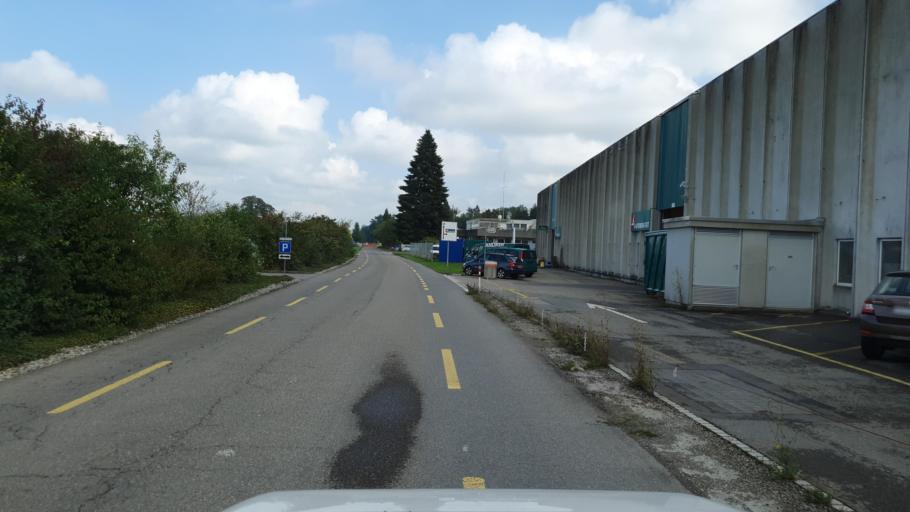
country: CH
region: Lucerne
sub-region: Lucerne-Land District
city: Ebikon
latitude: 47.0900
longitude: 8.3170
